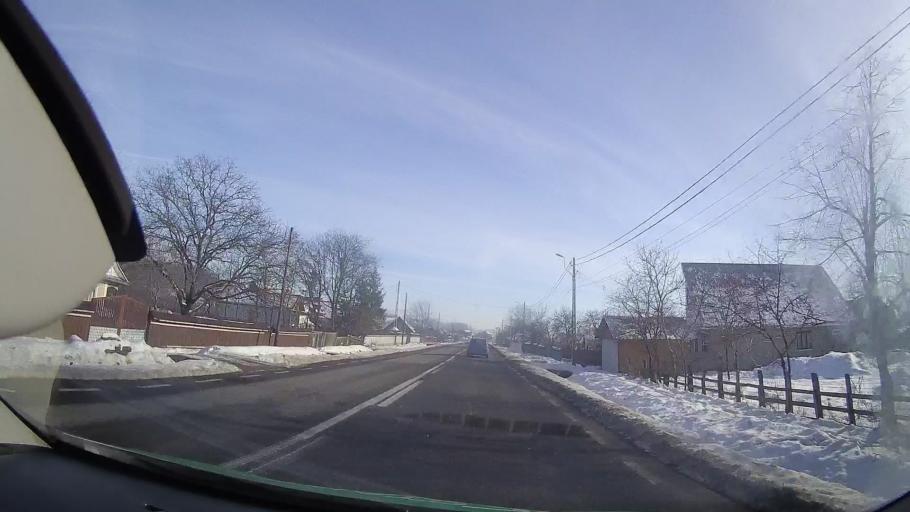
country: RO
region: Neamt
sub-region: Comuna Cracaoani
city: Cracaoani
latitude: 47.0889
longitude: 26.3263
